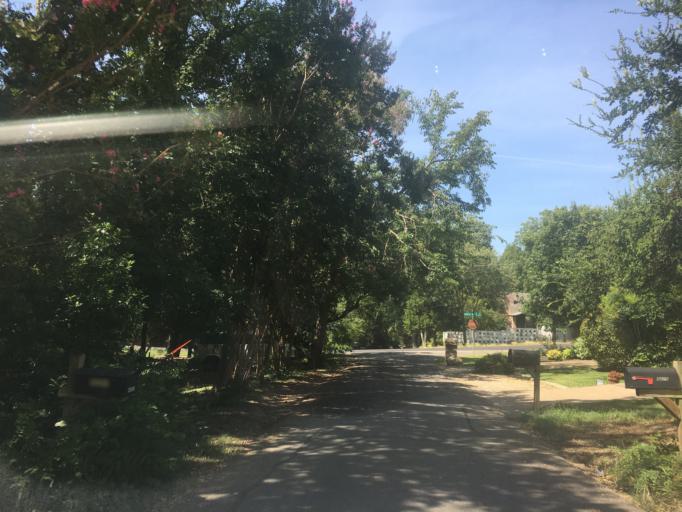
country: US
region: Texas
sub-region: Dallas County
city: Highland Park
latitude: 32.8671
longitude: -96.7245
